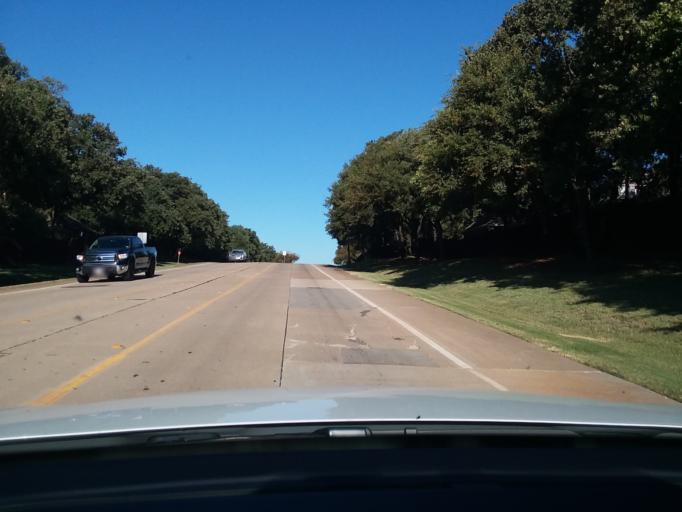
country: US
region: Texas
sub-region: Denton County
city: Highland Village
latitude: 33.0846
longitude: -97.0645
